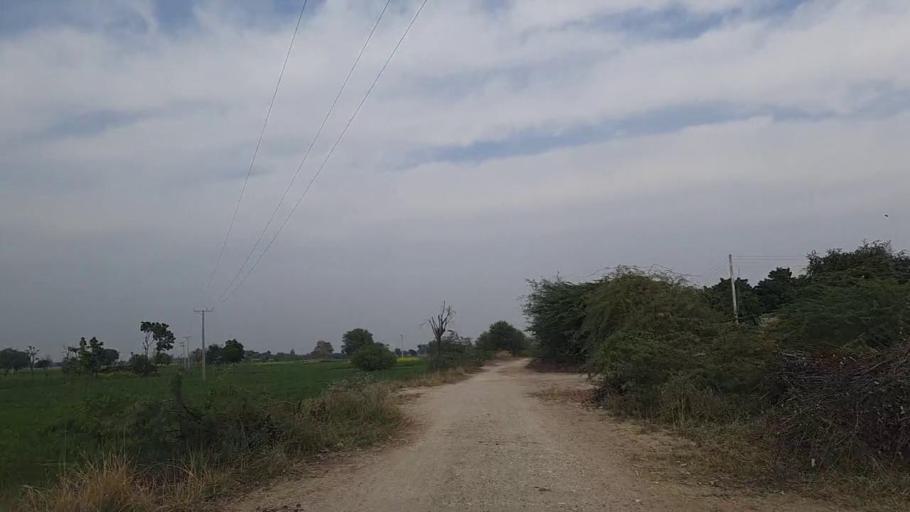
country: PK
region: Sindh
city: Daur
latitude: 26.4355
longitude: 68.4701
